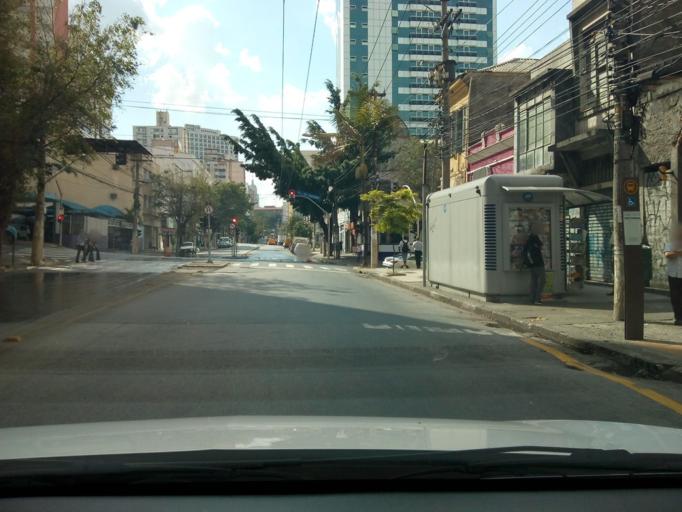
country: BR
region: Sao Paulo
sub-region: Sao Paulo
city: Sao Paulo
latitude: -23.5586
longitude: -46.6329
